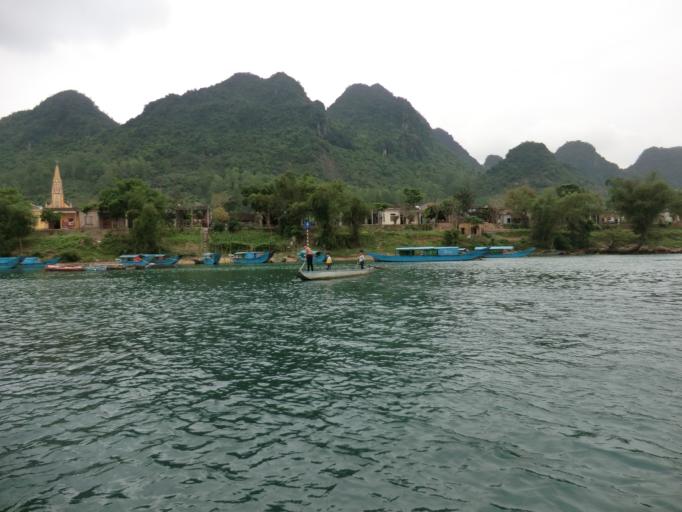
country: VN
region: Quang Binh
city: Ba Don
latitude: 17.6009
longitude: 106.2931
